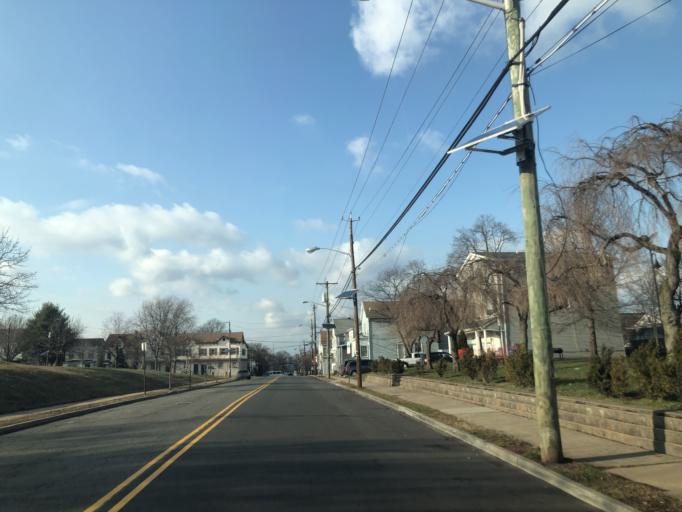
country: US
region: New Jersey
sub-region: Middlesex County
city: New Brunswick
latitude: 40.4846
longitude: -74.4433
